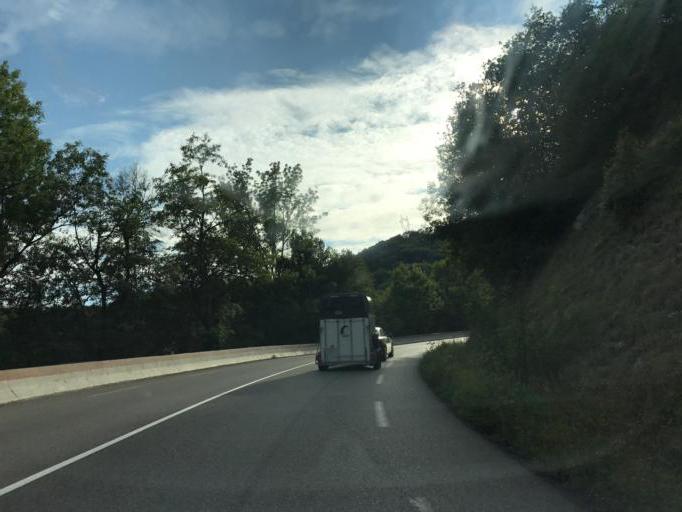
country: FR
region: Rhone-Alpes
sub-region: Departement de l'Ain
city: Collonges
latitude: 46.1104
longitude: 5.8783
